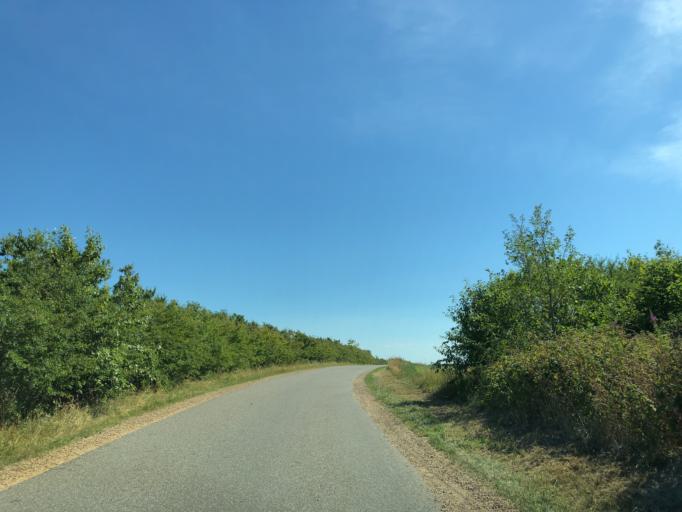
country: DK
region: Central Jutland
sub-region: Skive Kommune
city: Skive
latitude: 56.4593
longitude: 8.9766
